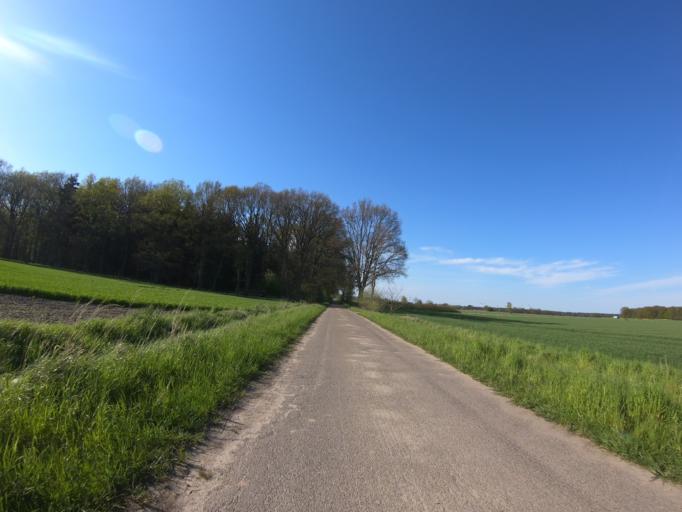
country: DE
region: Lower Saxony
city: Rotgesbuttel
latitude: 52.4026
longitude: 10.5334
